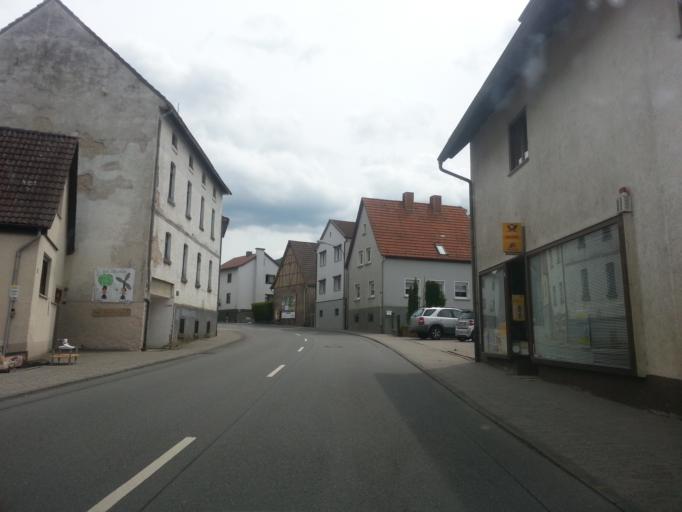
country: DE
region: Hesse
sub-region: Regierungsbezirk Darmstadt
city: Seeheim-Jugenheim
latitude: 49.7123
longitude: 8.6946
